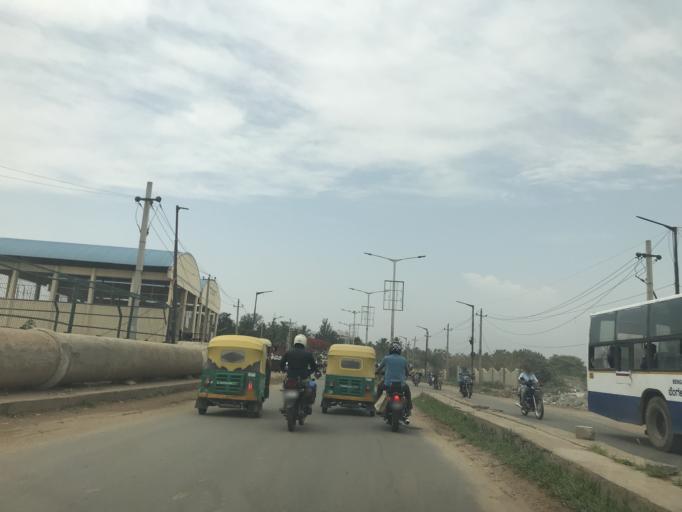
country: IN
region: Karnataka
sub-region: Bangalore Urban
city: Yelahanka
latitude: 13.0419
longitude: 77.6418
